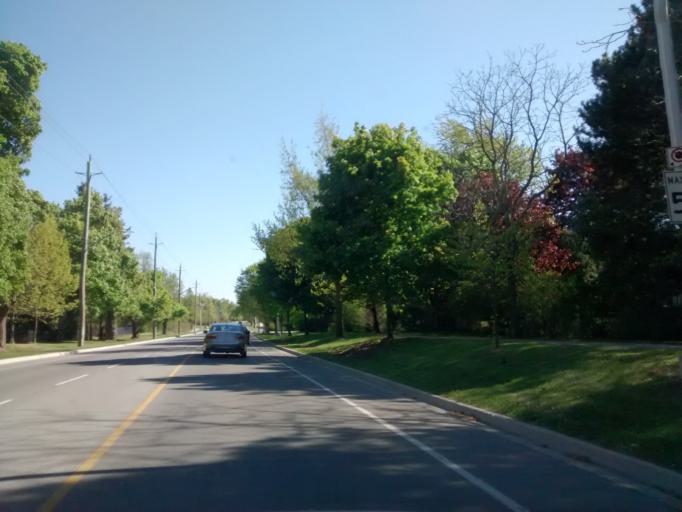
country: CA
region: Ontario
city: Oakville
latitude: 43.3838
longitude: -79.7173
